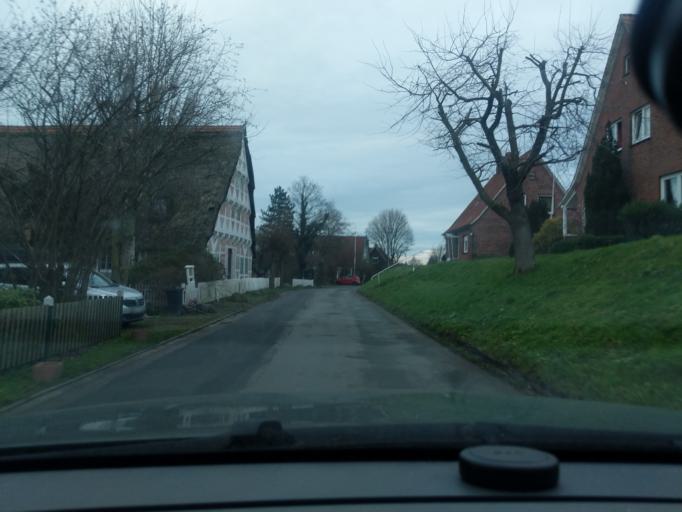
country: DE
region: Lower Saxony
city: Guderhandviertel
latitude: 53.5380
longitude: 9.6110
